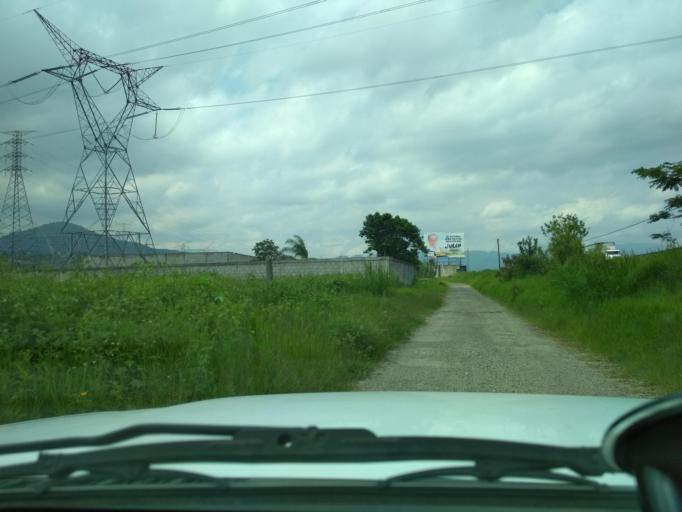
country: MX
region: Veracruz
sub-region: Ixtaczoquitlan
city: Buenavista
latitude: 18.8905
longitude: -97.0459
